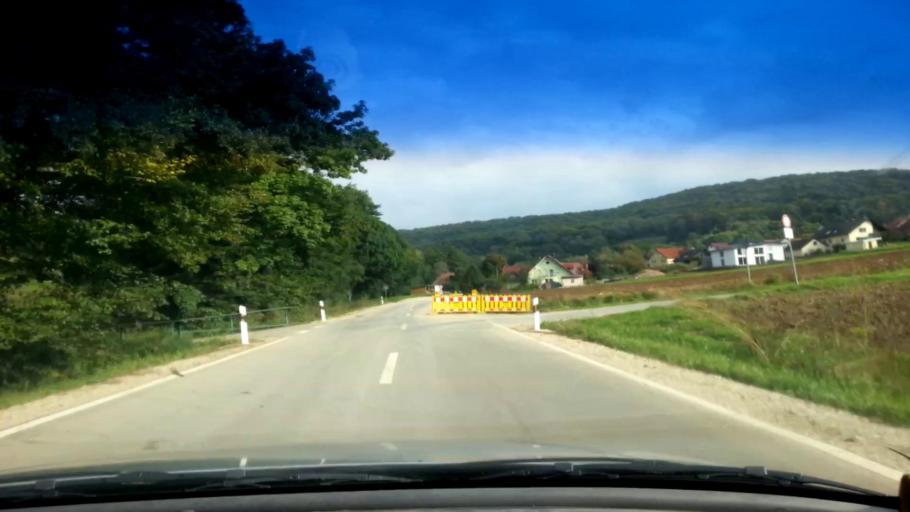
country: DE
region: Bavaria
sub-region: Upper Franconia
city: Schesslitz
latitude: 49.9979
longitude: 11.0742
